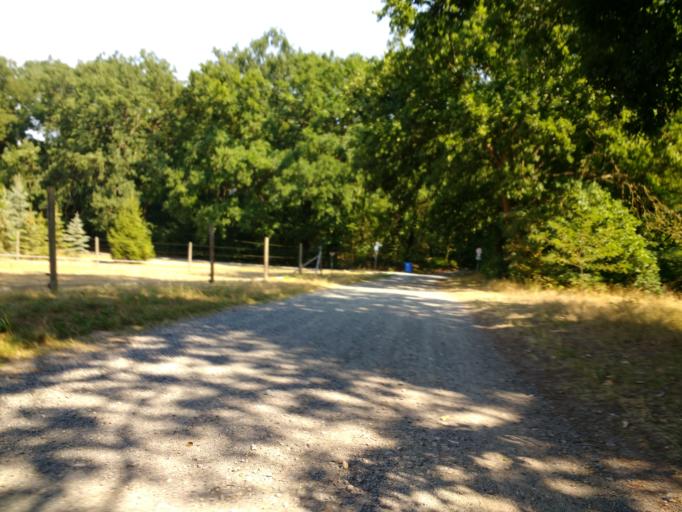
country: DE
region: Lower Saxony
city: Gifhorn
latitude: 52.4875
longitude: 10.5207
